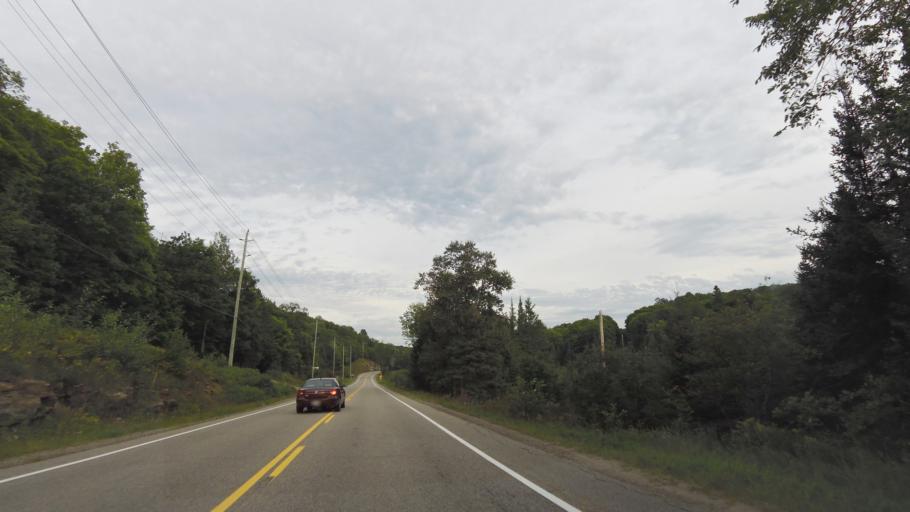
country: CA
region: Ontario
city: Bancroft
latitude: 45.0218
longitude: -78.3599
